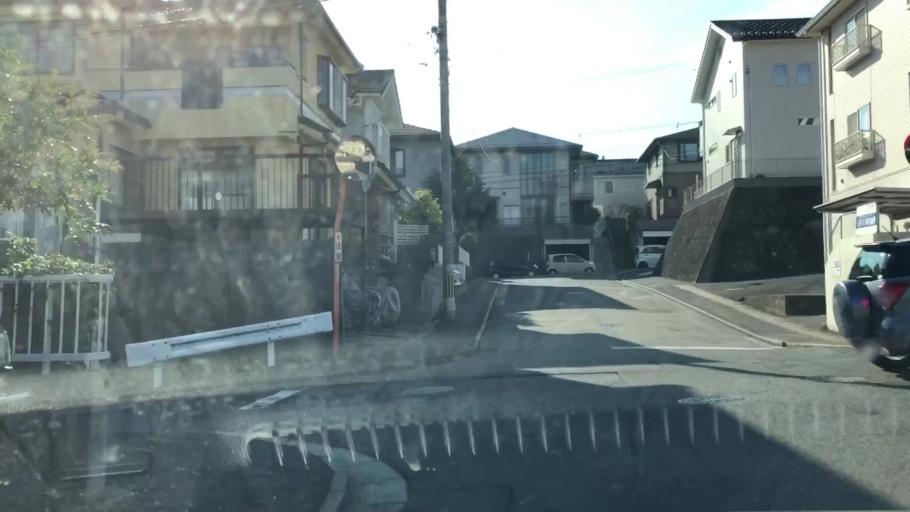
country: JP
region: Hiroshima
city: Hiroshima-shi
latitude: 34.4025
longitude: 132.4136
